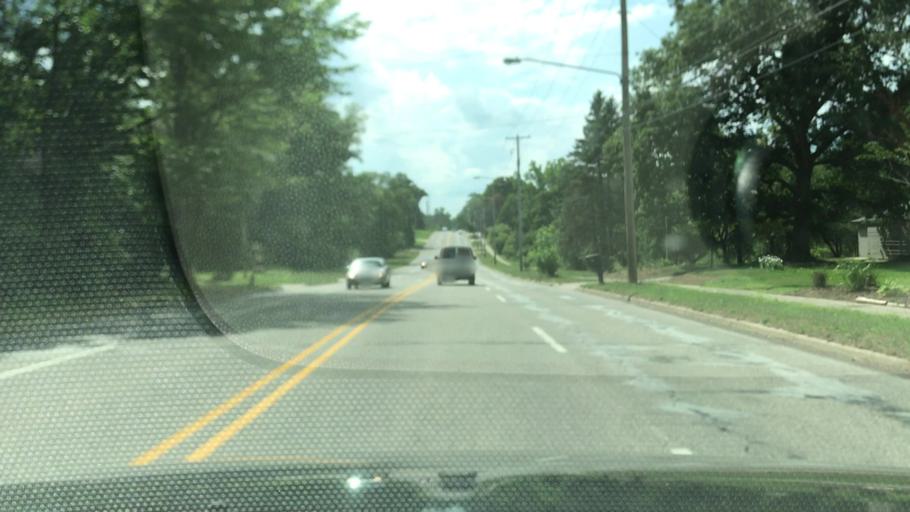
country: US
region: Michigan
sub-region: Kent County
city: East Grand Rapids
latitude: 42.9699
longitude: -85.5954
